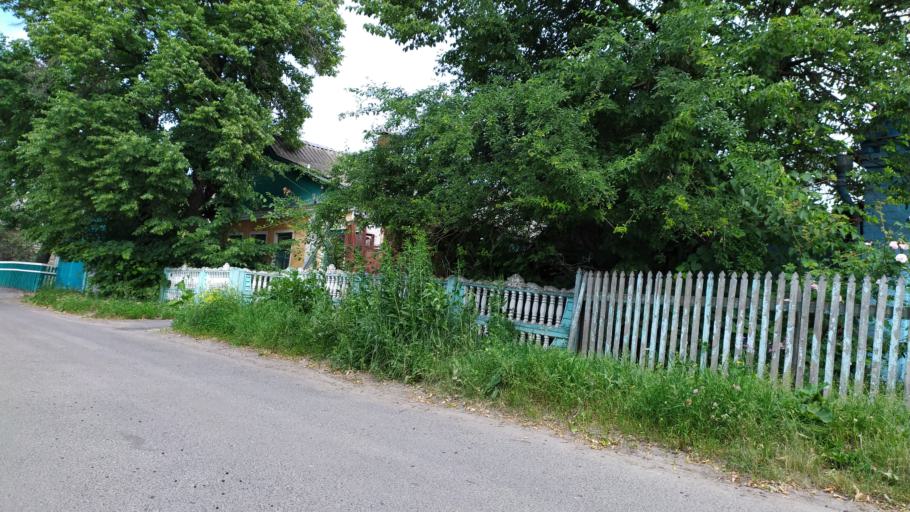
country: RU
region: Kursk
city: Kursk
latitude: 51.6619
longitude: 36.1537
